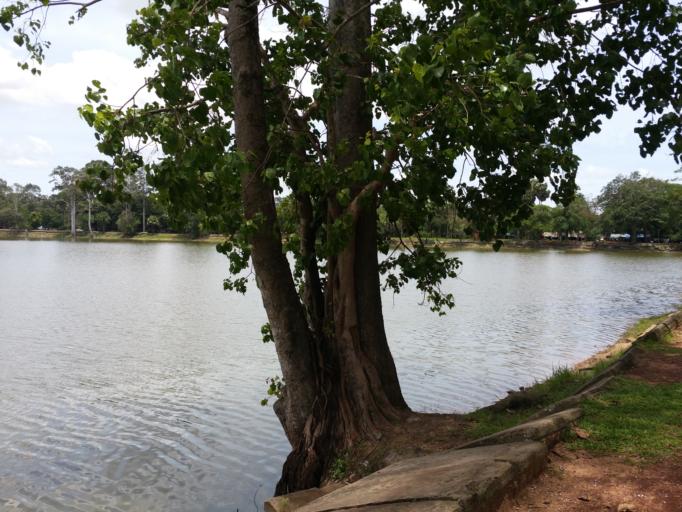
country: KH
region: Siem Reap
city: Siem Reap
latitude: 13.4090
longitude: 103.8596
